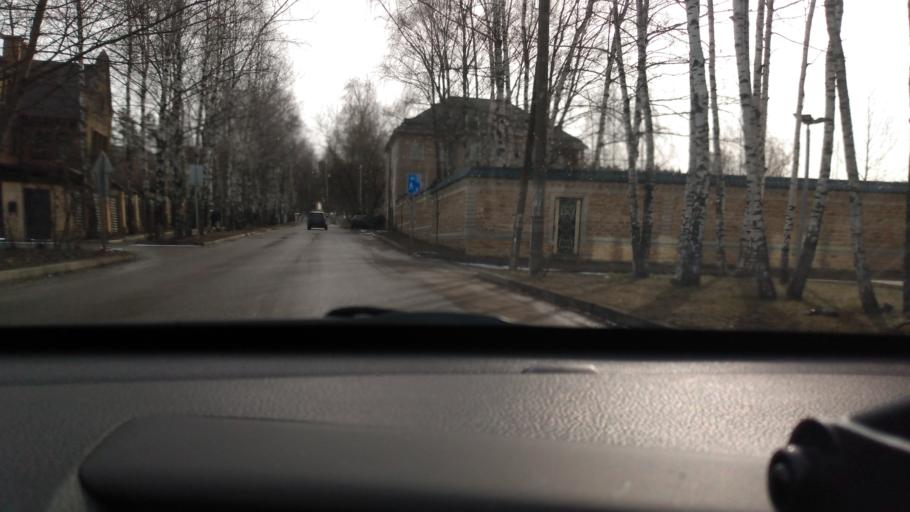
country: RU
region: Moskovskaya
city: Barvikha
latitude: 55.7348
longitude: 37.2499
